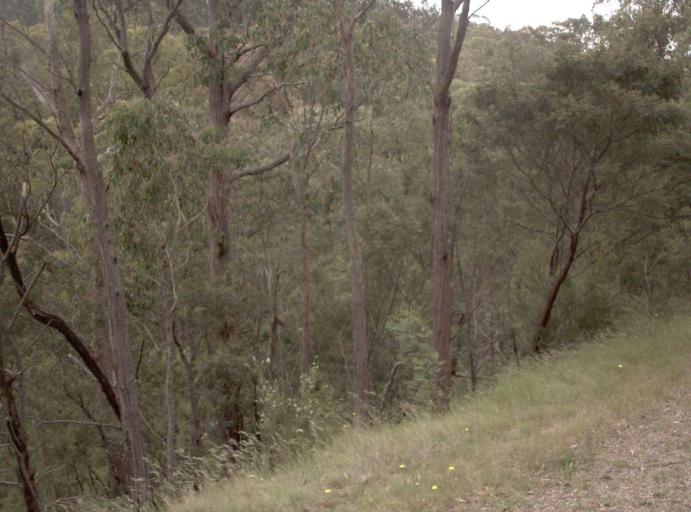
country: AU
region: Victoria
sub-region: East Gippsland
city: Bairnsdale
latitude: -37.4752
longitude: 147.2139
